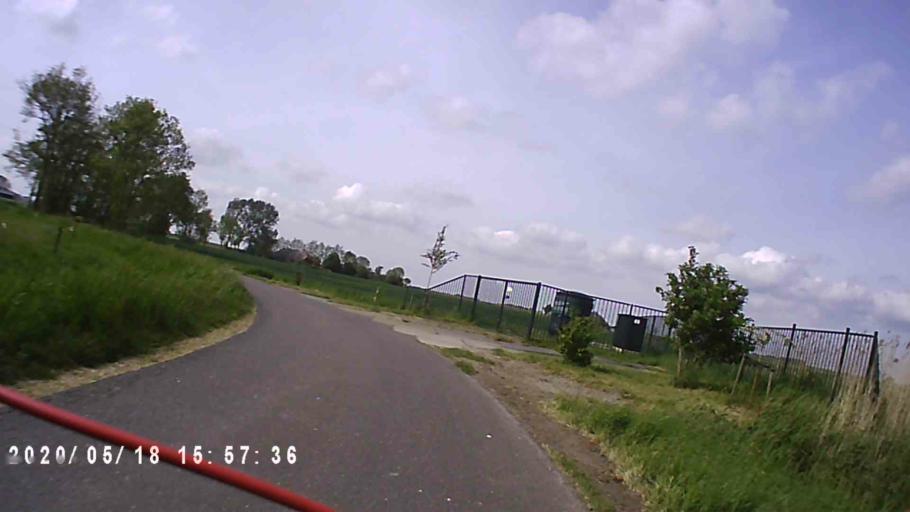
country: NL
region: Groningen
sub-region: Gemeente Zuidhorn
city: Oldehove
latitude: 53.3121
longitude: 6.4428
